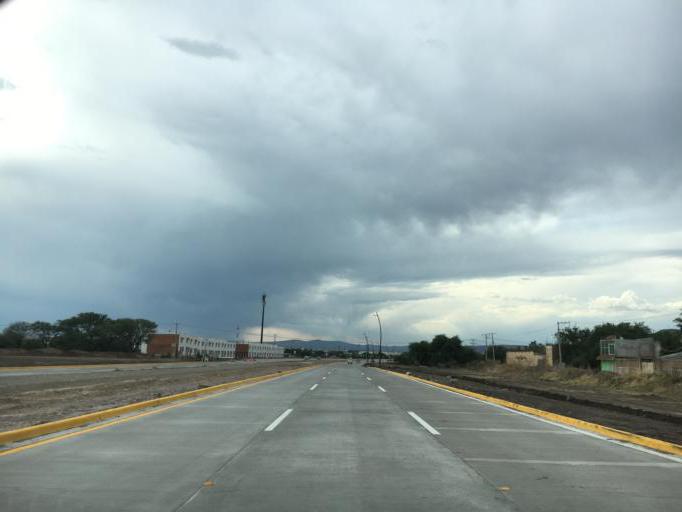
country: MX
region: Guanajuato
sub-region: Leon
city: Fraccionamiento Paraiso Real
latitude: 21.1117
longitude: -101.5865
